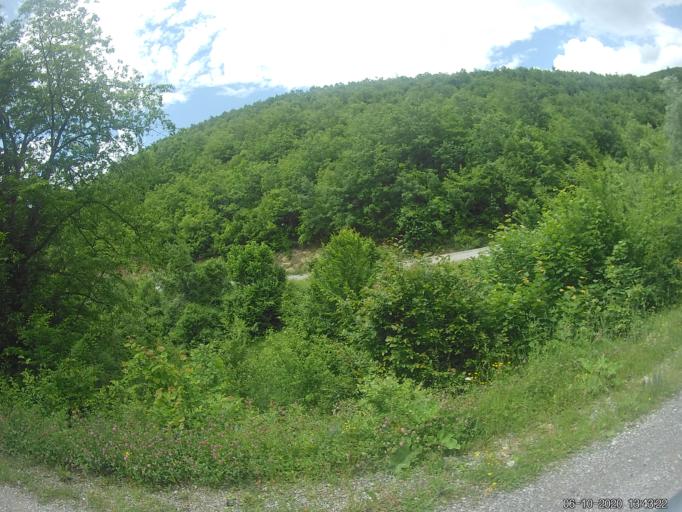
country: XK
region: Prizren
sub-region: Komuna e Therandes
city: Budakovo
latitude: 42.4161
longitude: 20.9184
